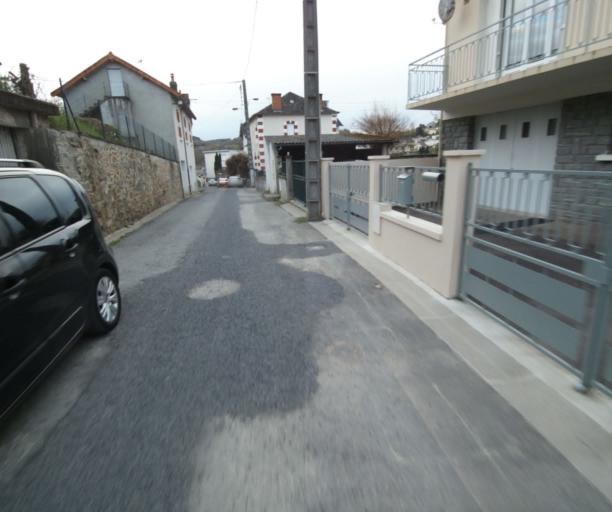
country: FR
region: Limousin
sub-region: Departement de la Correze
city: Tulle
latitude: 45.2600
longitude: 1.7572
